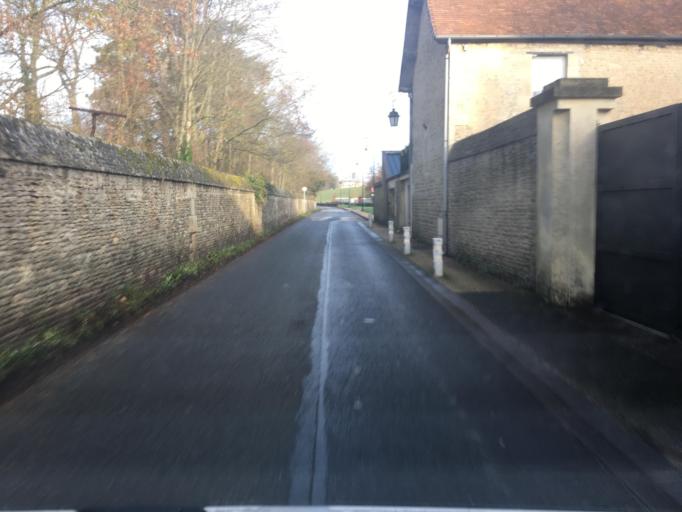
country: FR
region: Lower Normandy
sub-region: Departement du Calvados
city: Rots
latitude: 49.2005
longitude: -0.4772
